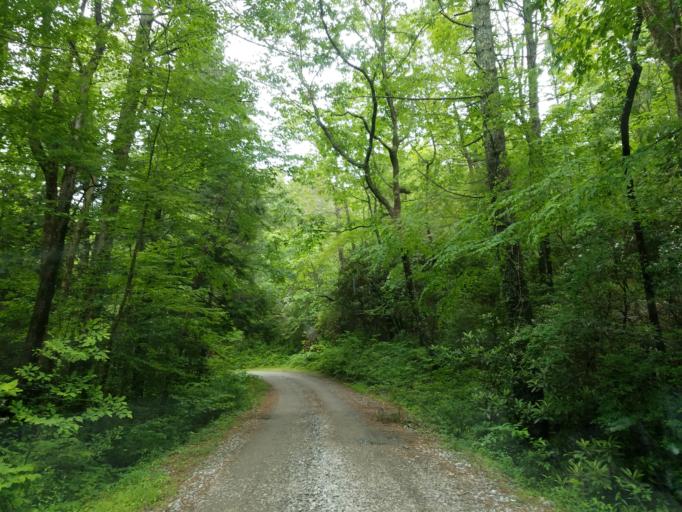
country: US
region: Georgia
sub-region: Lumpkin County
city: Dahlonega
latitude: 34.6723
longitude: -83.9764
